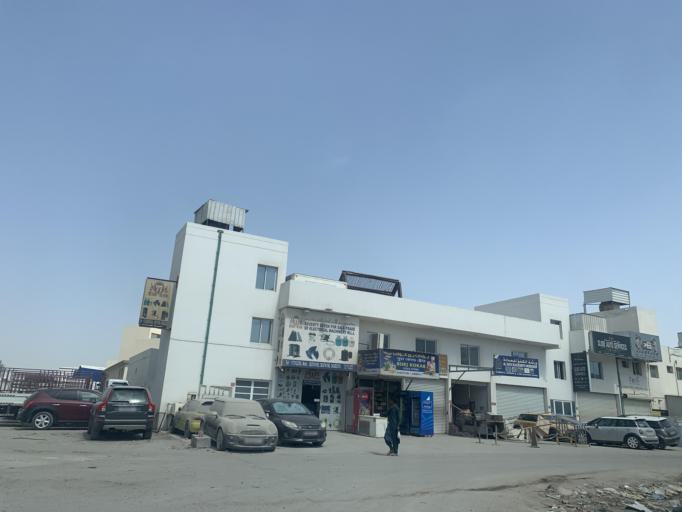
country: BH
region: Central Governorate
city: Madinat Hamad
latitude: 26.1398
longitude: 50.4842
